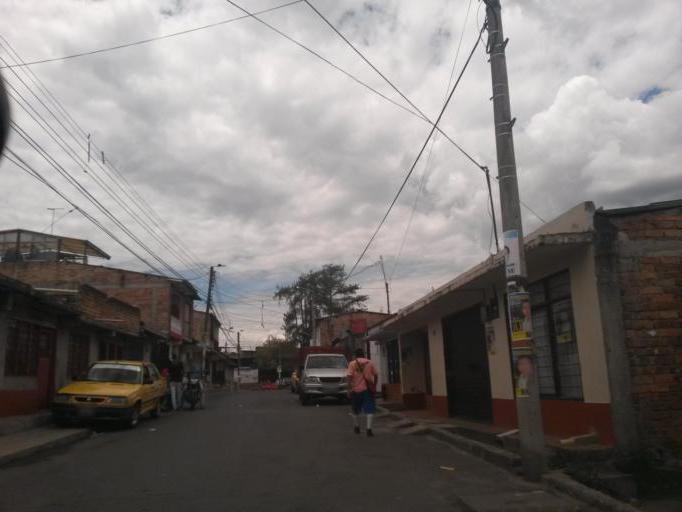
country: CO
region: Cauca
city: Popayan
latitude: 2.4493
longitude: -76.6300
